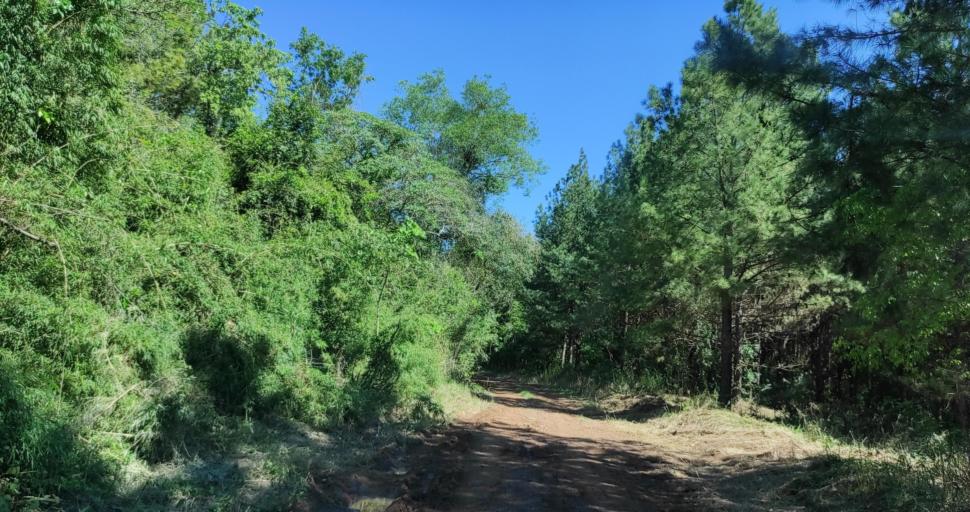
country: AR
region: Misiones
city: Ruiz de Montoya
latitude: -26.9512
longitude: -54.9812
